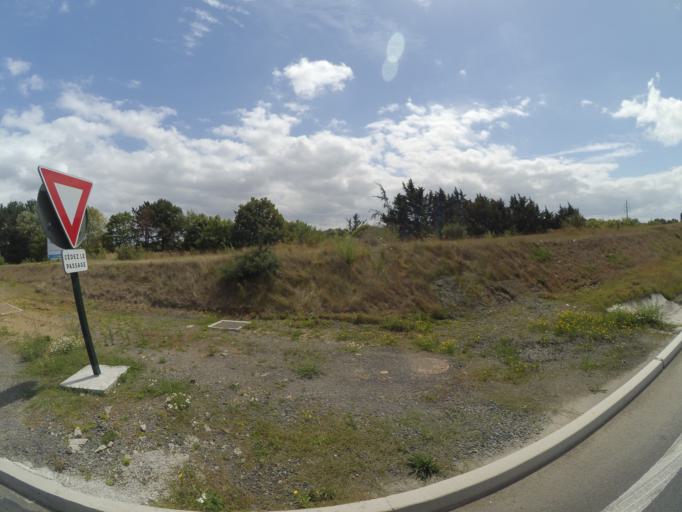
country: FR
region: Brittany
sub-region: Departement des Cotes-d'Armor
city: Yffiniac
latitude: 48.4811
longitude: -2.6983
